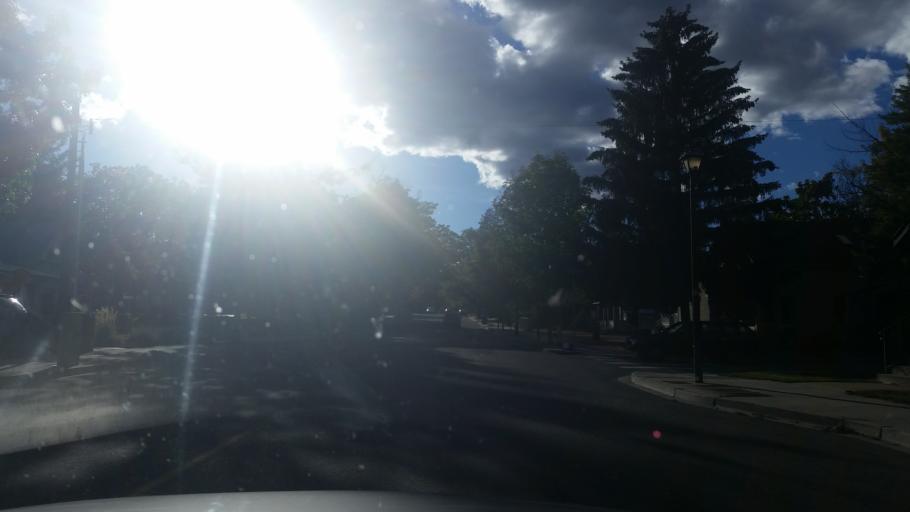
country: US
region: Washington
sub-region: Chelan County
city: Cashmere
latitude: 47.5208
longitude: -120.4596
